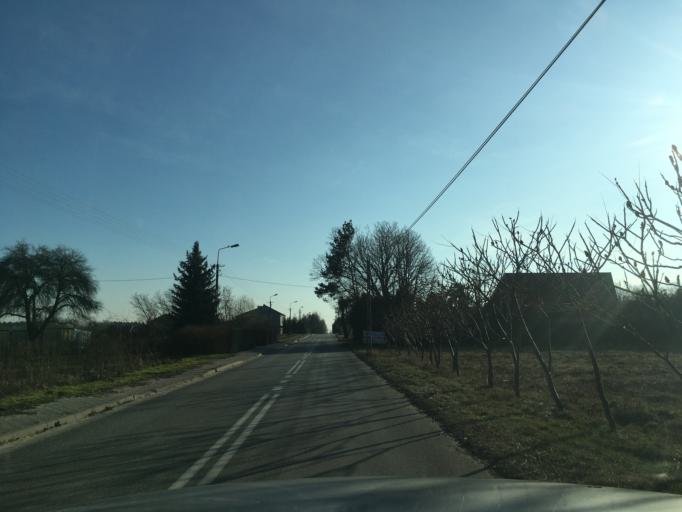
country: PL
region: Masovian Voivodeship
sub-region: Powiat pruszkowski
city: Nadarzyn
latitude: 52.0481
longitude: 20.8260
